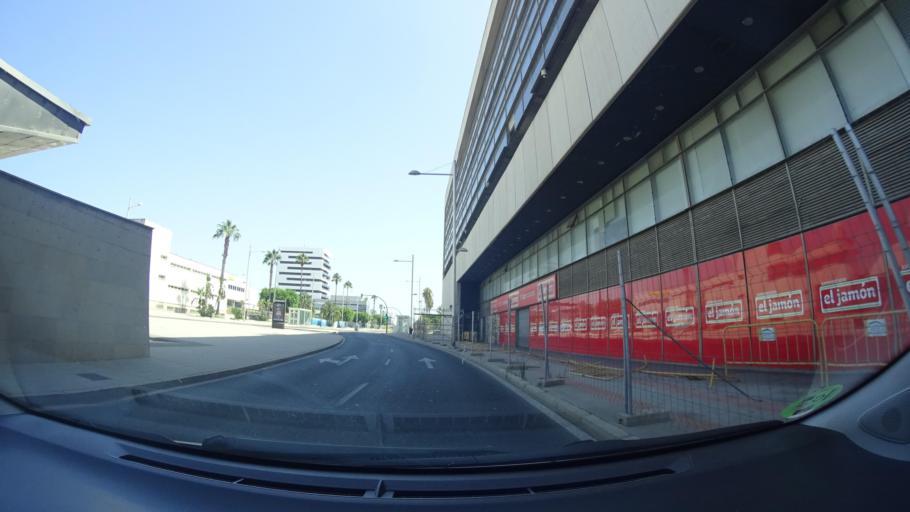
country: ES
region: Andalusia
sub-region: Provincia de Cadiz
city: Cadiz
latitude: 36.5030
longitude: -6.2722
